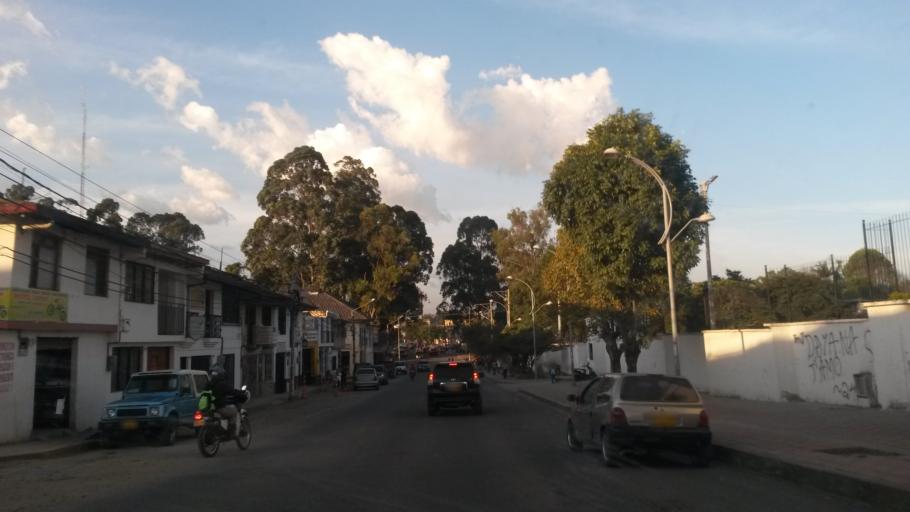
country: CO
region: Cauca
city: Popayan
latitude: 2.4445
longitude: -76.6097
